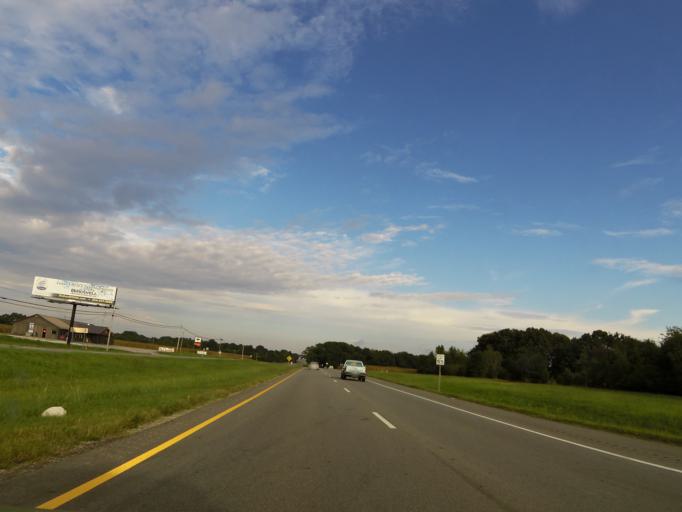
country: US
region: Alabama
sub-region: Lauderdale County
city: Rogersville
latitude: 34.8286
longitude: -87.3119
